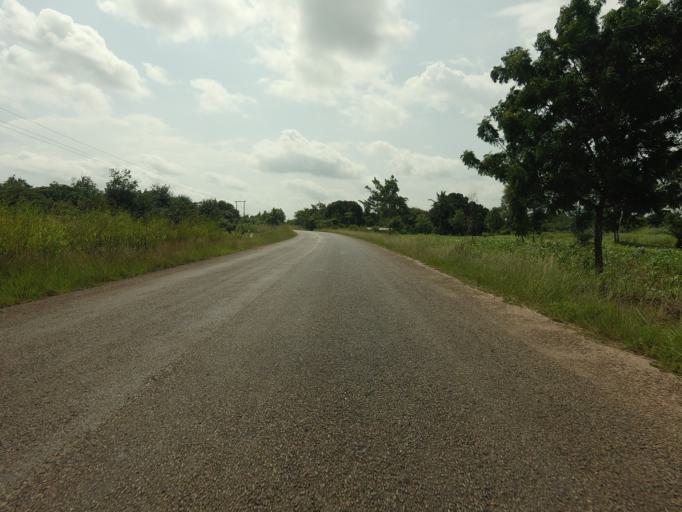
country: TG
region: Maritime
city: Lome
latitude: 6.2625
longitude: 0.9564
